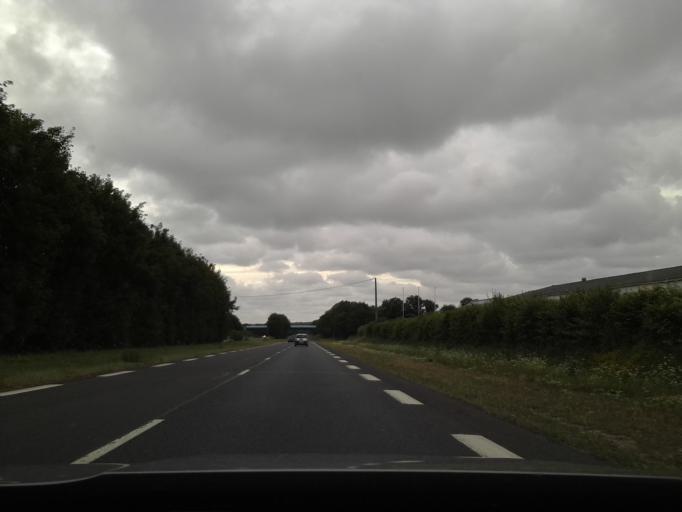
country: FR
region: Lower Normandy
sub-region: Departement du Calvados
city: Le Molay-Littry
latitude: 49.3255
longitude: -0.8764
